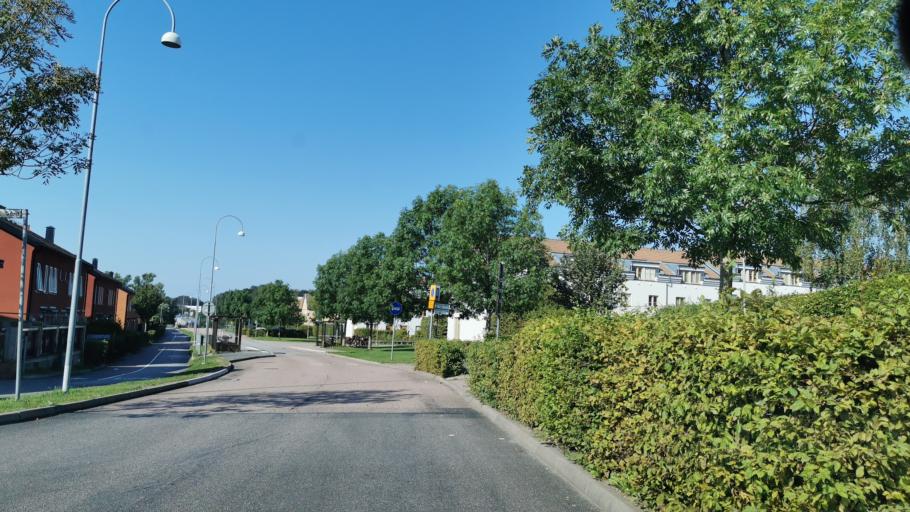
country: SE
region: Vaestra Goetaland
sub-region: Molndal
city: Moelndal
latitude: 57.6510
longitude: 11.9651
